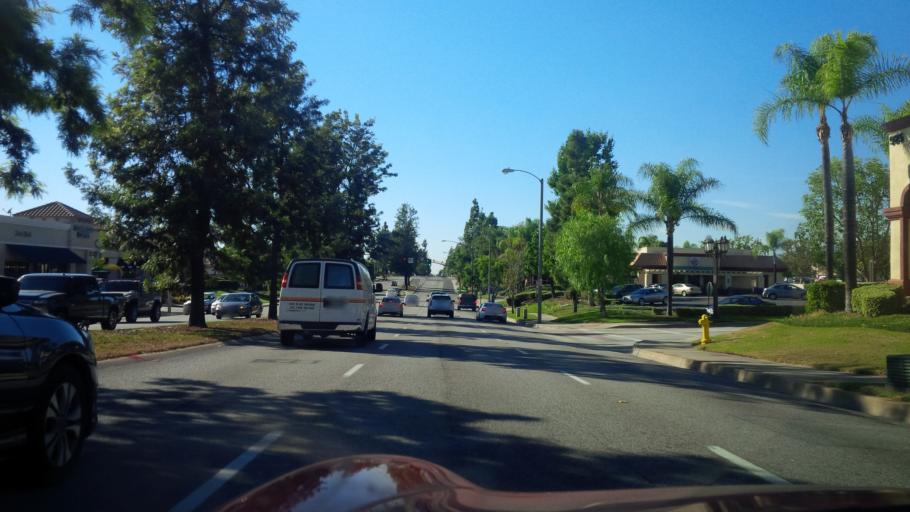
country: US
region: California
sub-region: Los Angeles County
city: San Dimas
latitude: 34.1068
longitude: -117.8254
